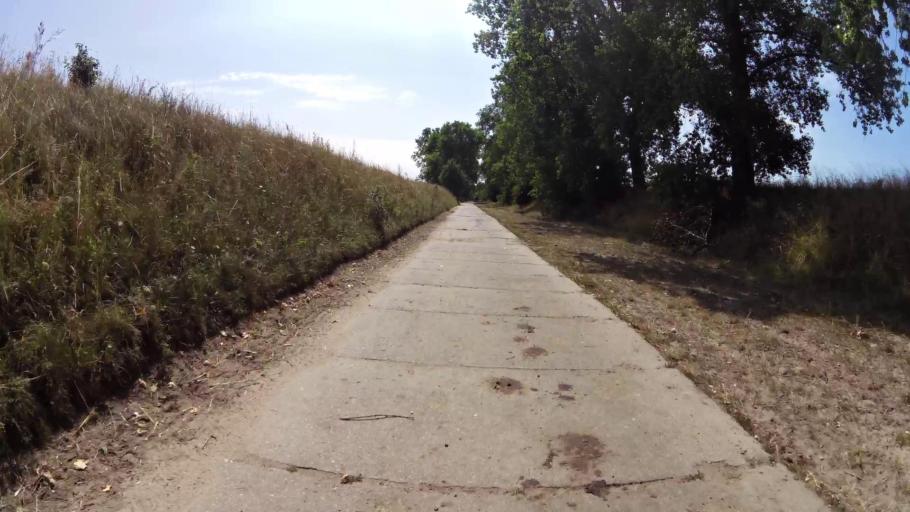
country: PL
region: West Pomeranian Voivodeship
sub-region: Powiat stargardzki
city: Suchan
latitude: 53.2620
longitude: 15.4033
